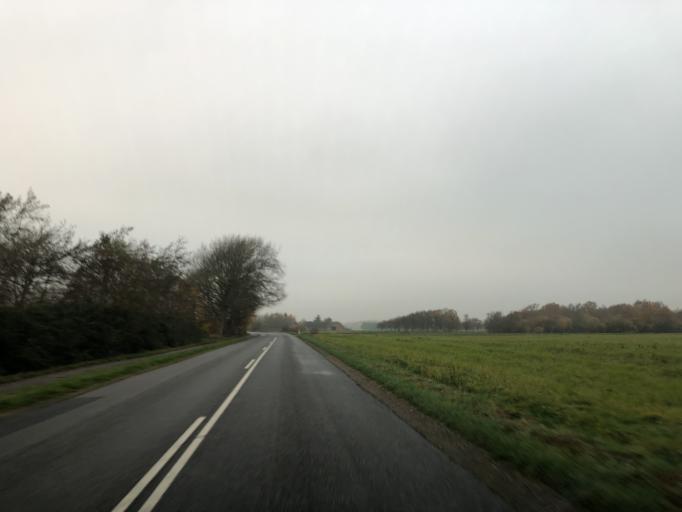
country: DK
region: Central Jutland
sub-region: Herning Kommune
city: Vildbjerg
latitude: 56.2137
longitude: 8.7493
